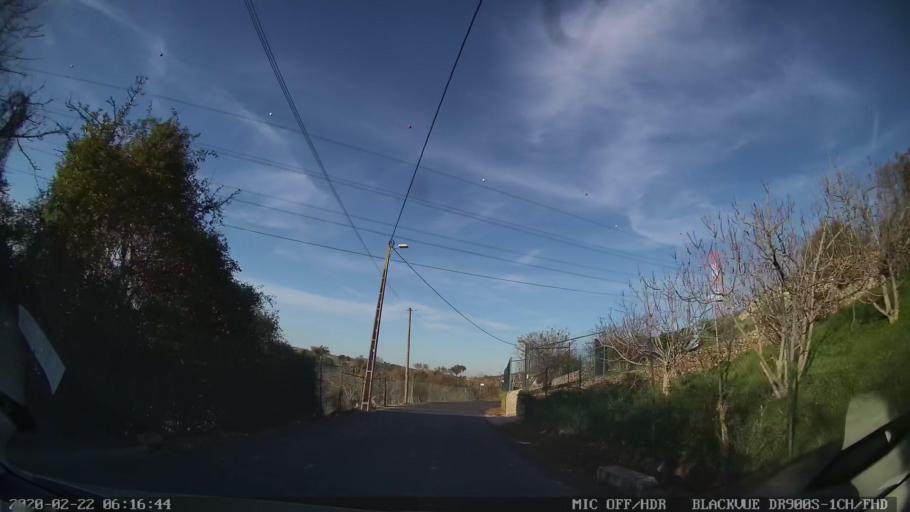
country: PT
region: Lisbon
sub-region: Vila Franca de Xira
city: Castanheira do Ribatejo
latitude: 38.9930
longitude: -9.0165
